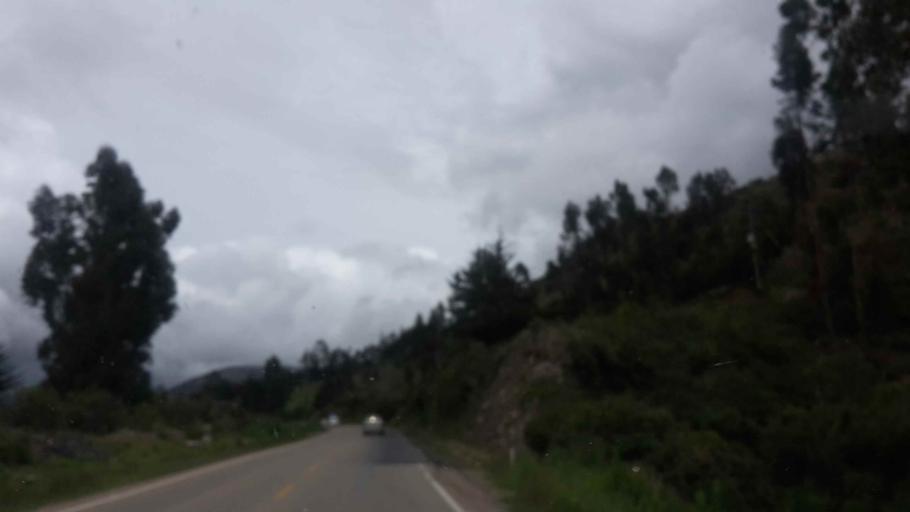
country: BO
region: Cochabamba
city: Arani
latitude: -17.4777
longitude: -65.4930
